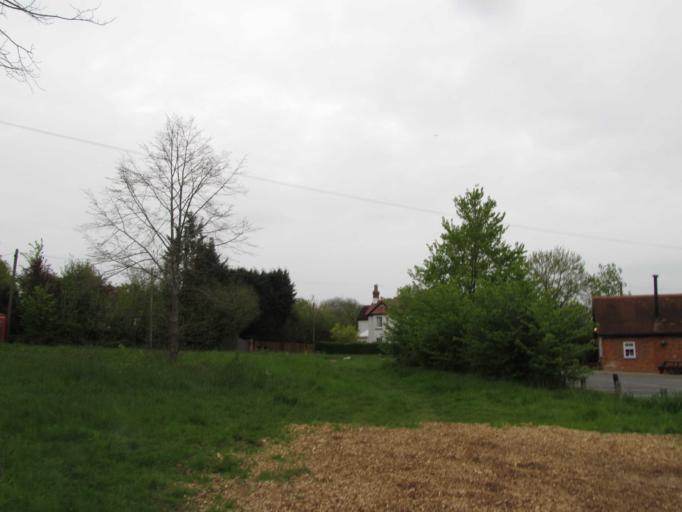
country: GB
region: England
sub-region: Royal Borough of Windsor and Maidenhead
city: Bisham
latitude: 51.5395
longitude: -0.7618
